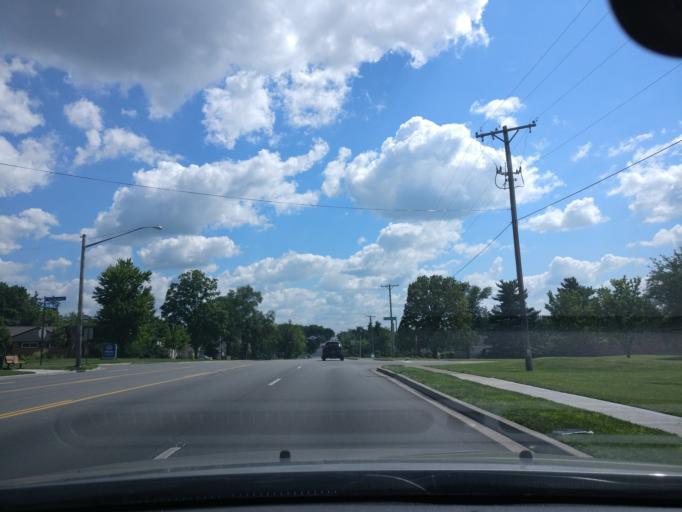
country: US
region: Ohio
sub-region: Montgomery County
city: Centerville
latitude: 39.6418
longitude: -84.1579
